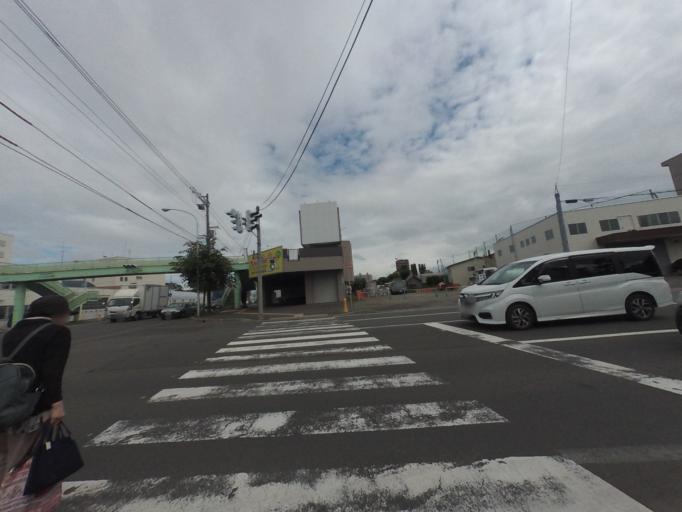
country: JP
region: Hokkaido
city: Sapporo
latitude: 43.0619
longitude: 141.3852
